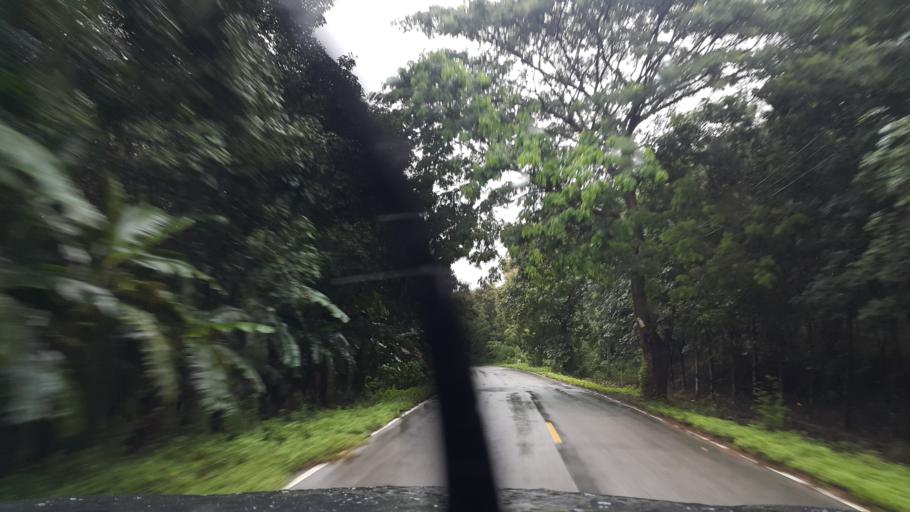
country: TH
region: Phayao
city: Phu Sang
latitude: 19.6106
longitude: 100.4079
